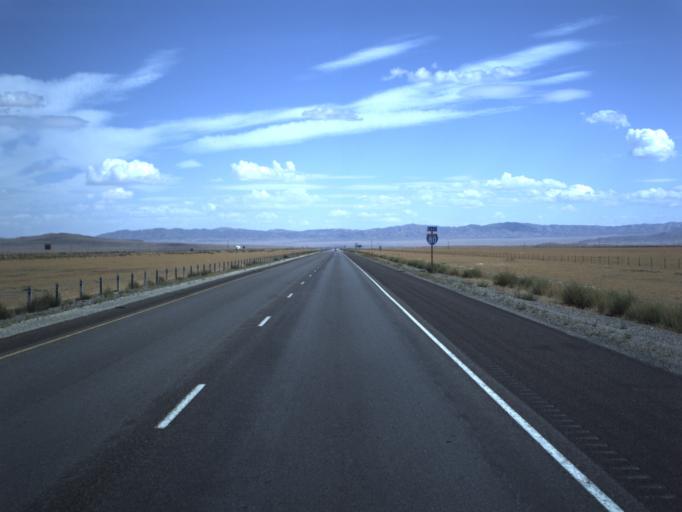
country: US
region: Utah
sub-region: Tooele County
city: Wendover
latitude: 40.7263
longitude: -113.2472
